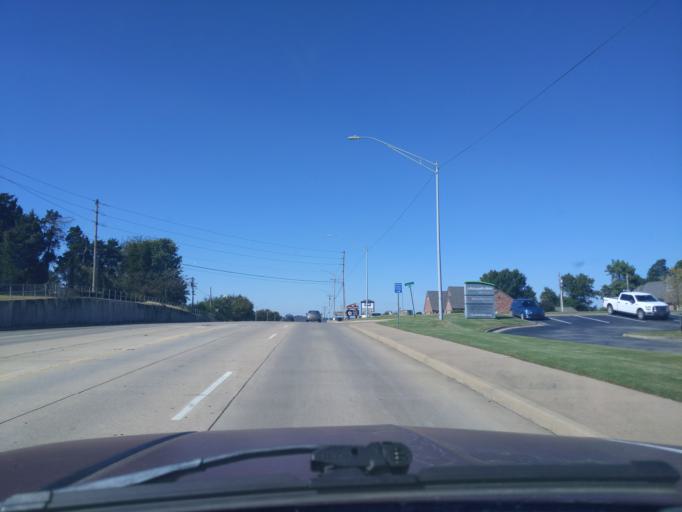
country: US
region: Oklahoma
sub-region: Creek County
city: Sapulpa
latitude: 35.9885
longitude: -96.0938
